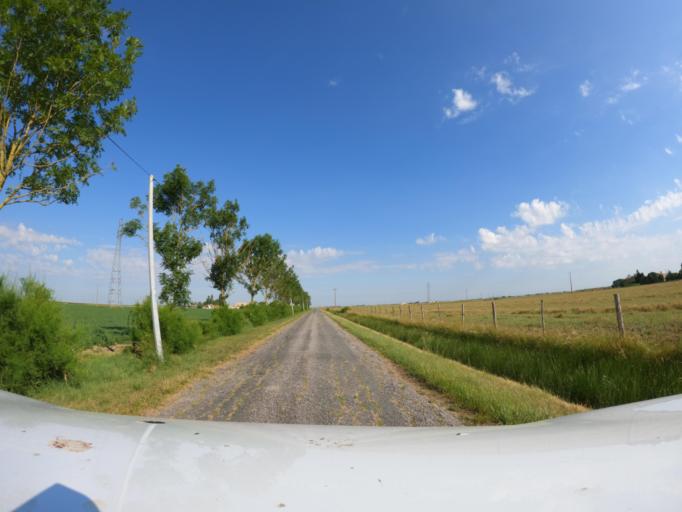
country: FR
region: Poitou-Charentes
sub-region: Departement de la Charente-Maritime
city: Charron
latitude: 46.3228
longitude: -1.0834
